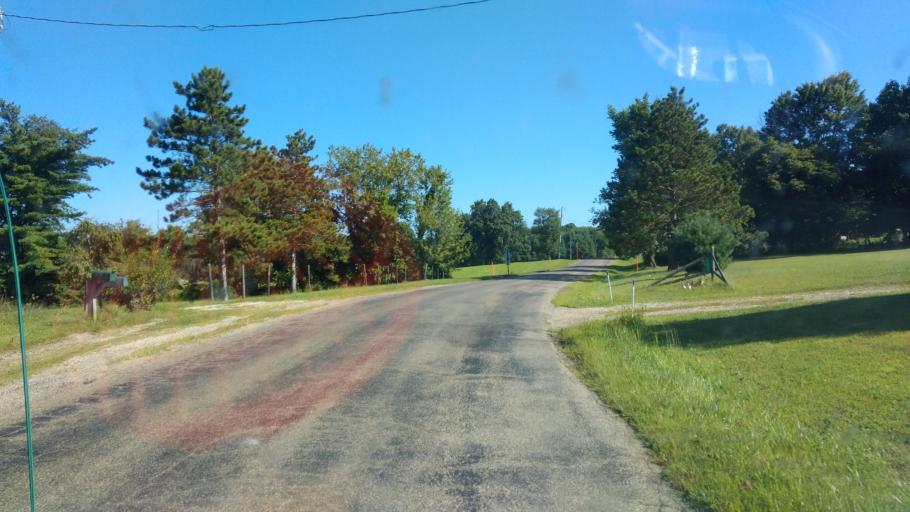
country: US
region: Ohio
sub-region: Knox County
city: Mount Vernon
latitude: 40.4580
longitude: -82.4347
